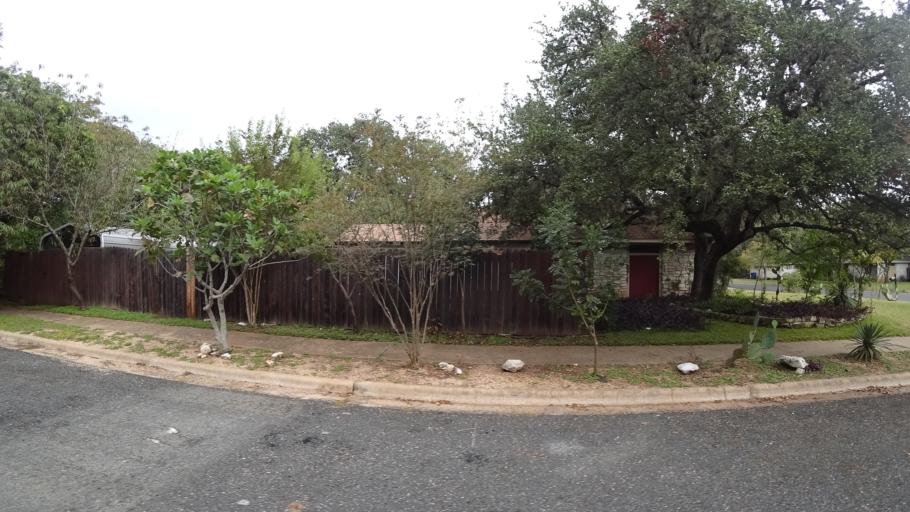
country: US
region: Texas
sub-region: Travis County
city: Shady Hollow
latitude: 30.2170
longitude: -97.8363
